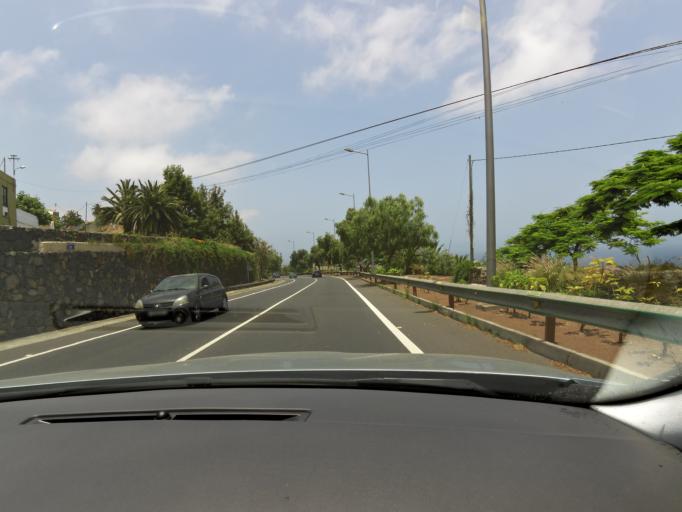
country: ES
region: Canary Islands
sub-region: Provincia de Santa Cruz de Tenerife
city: La Orotava
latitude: 28.4065
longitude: -16.5287
